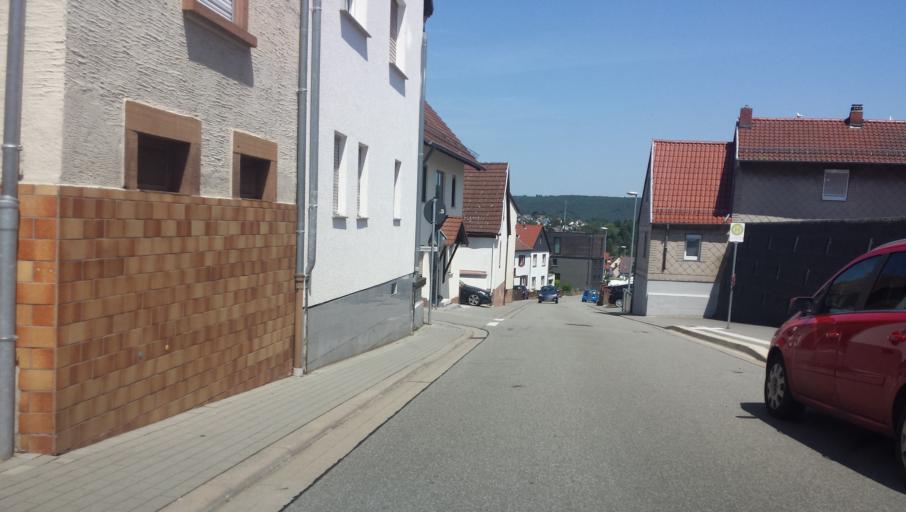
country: DE
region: Rheinland-Pfalz
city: Hochspeyer
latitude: 49.4389
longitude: 7.8920
